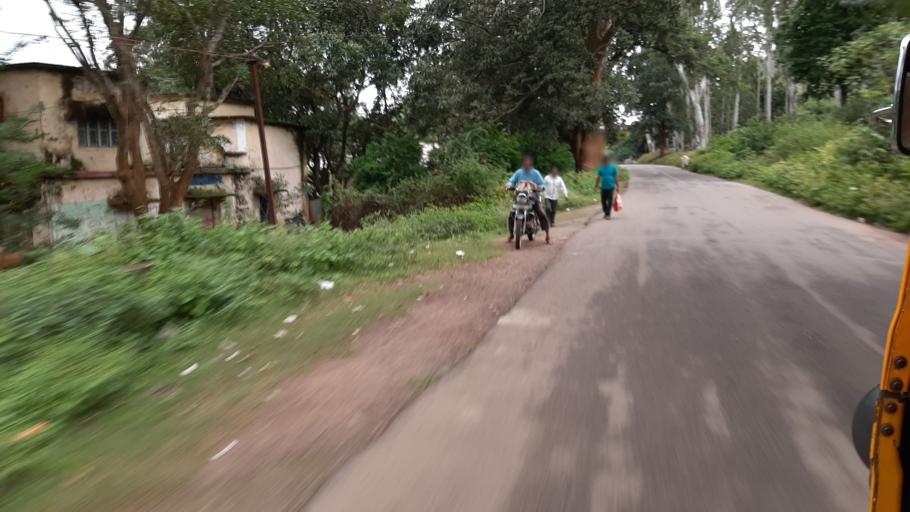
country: IN
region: Andhra Pradesh
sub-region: Vizianagaram District
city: Salur
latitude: 18.2369
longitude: 83.0058
